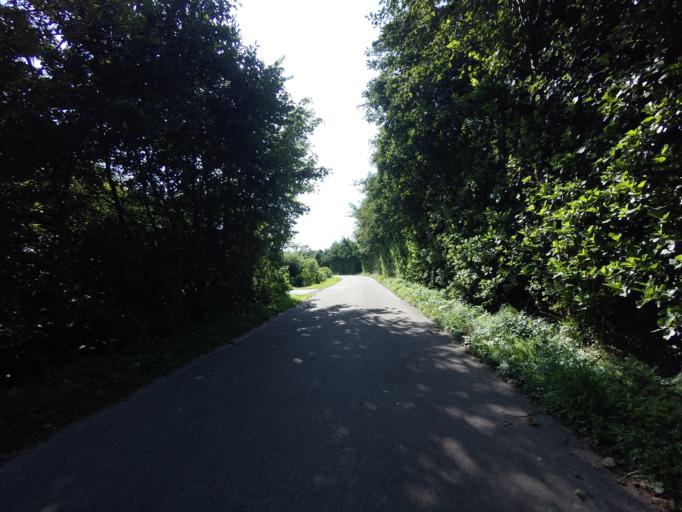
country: NL
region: Friesland
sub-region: Gemeente Terschelling
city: West-Terschelling
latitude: 53.3923
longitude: 5.3007
